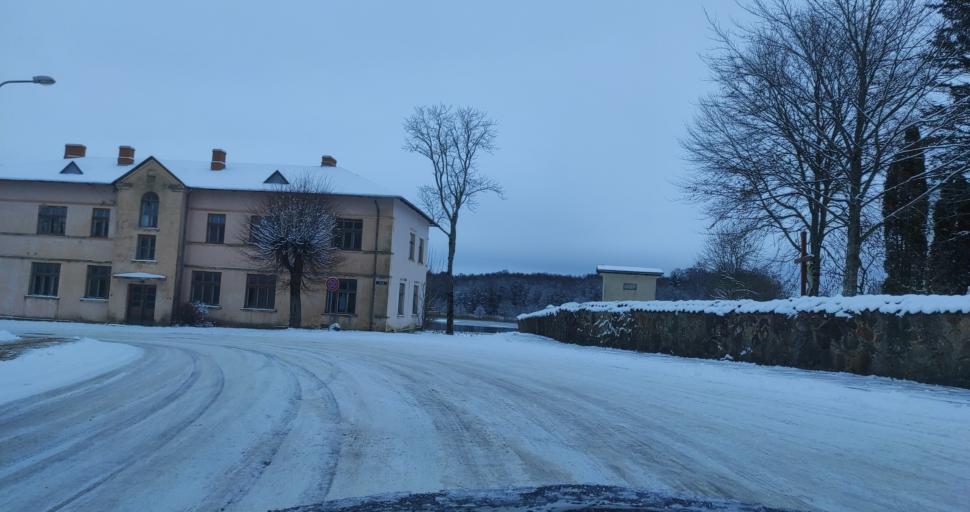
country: LV
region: Alsunga
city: Alsunga
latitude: 56.9797
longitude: 21.5699
